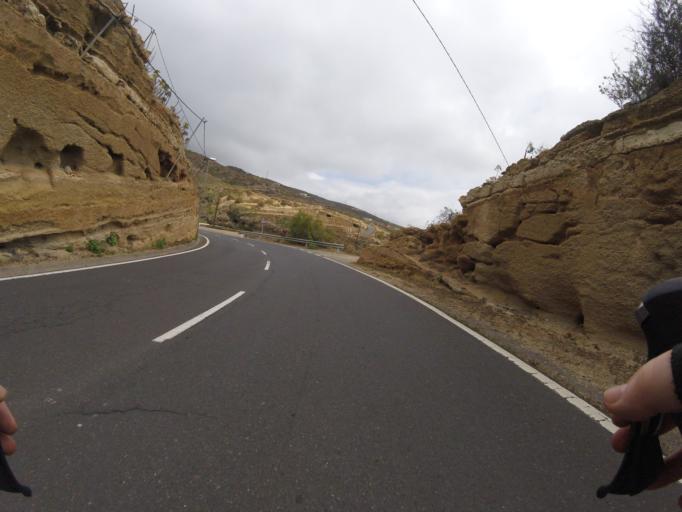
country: ES
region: Canary Islands
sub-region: Provincia de Santa Cruz de Tenerife
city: Guimar
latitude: 28.2746
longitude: -16.4133
